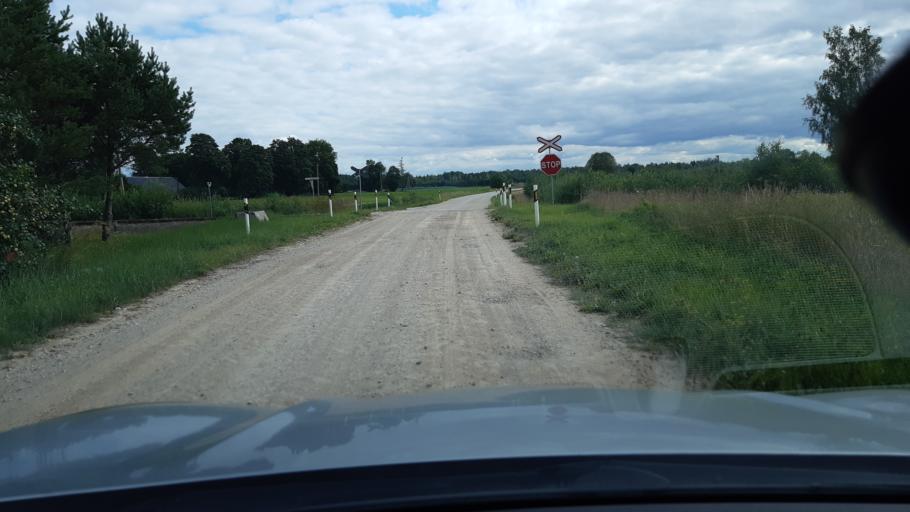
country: EE
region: Paernumaa
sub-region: Vaendra vald (alev)
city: Vandra
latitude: 58.7943
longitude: 24.9982
